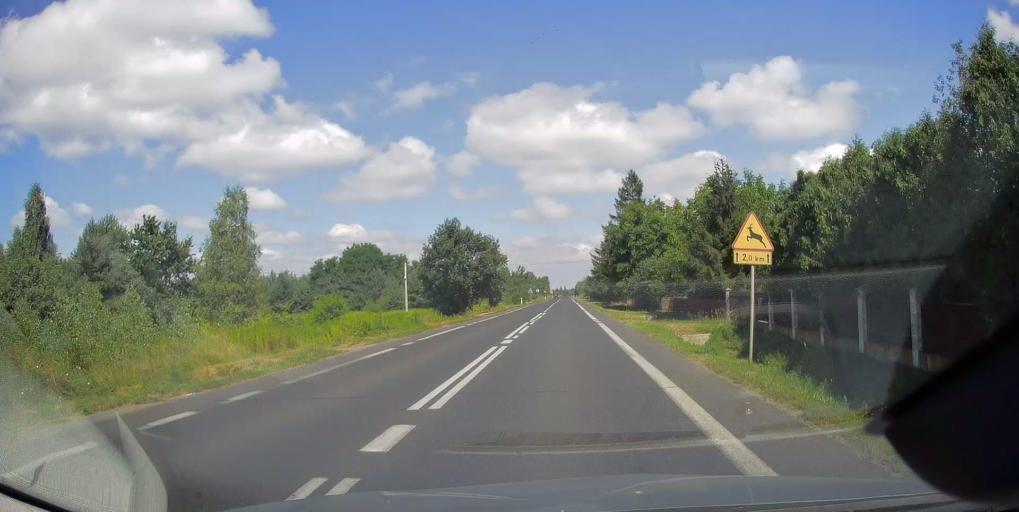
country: PL
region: Subcarpathian Voivodeship
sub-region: Powiat debicki
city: Brzeznica
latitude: 50.1334
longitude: 21.4857
